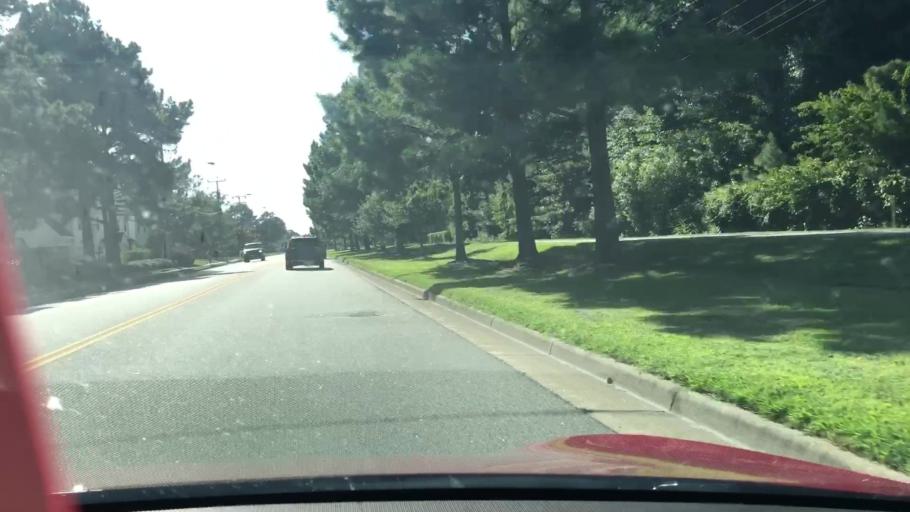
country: US
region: Virginia
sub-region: City of Virginia Beach
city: Virginia Beach
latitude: 36.8379
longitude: -75.9933
